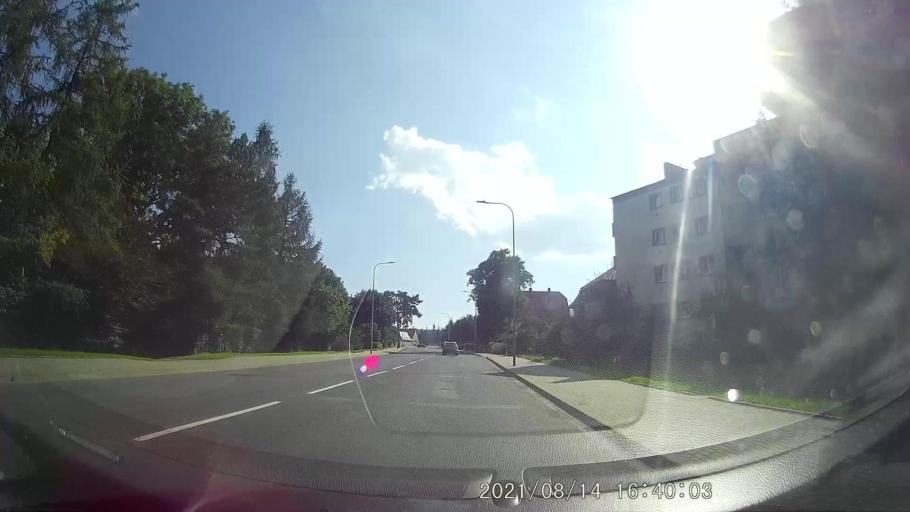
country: PL
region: Lower Silesian Voivodeship
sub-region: Powiat kamiennogorski
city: Kamienna Gora
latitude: 50.7821
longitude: 16.0197
